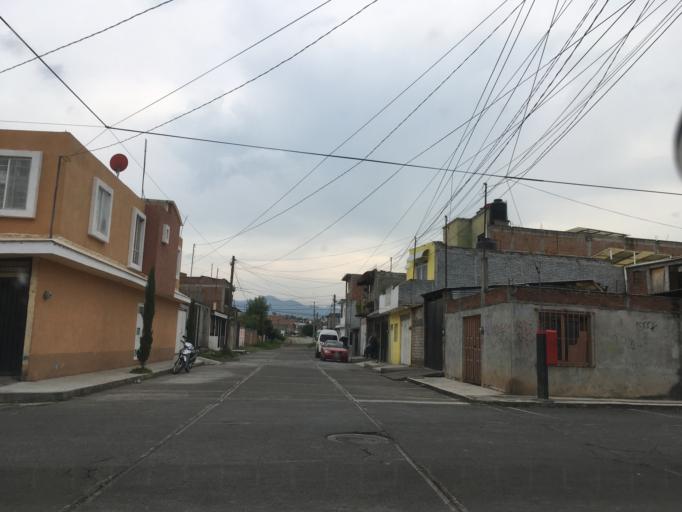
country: MX
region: Michoacan
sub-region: Morelia
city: San Antonio
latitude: 19.6938
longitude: -101.2315
